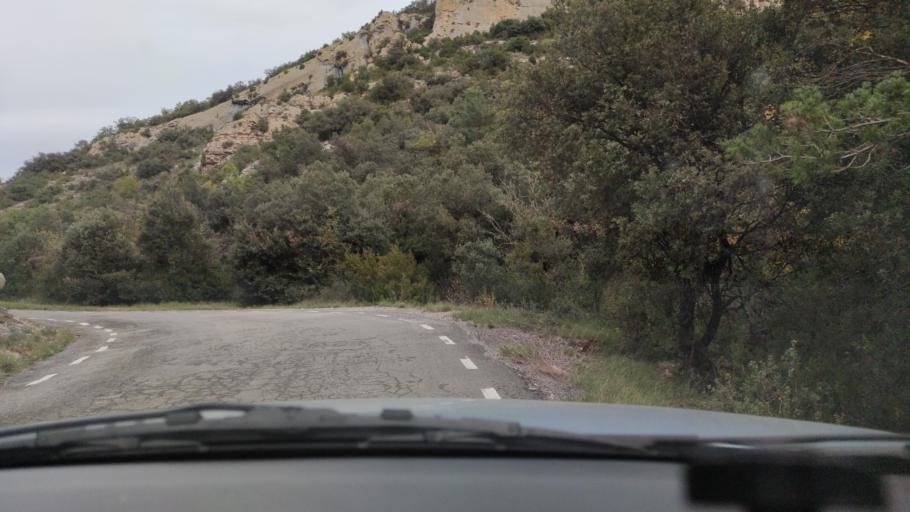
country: ES
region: Catalonia
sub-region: Provincia de Lleida
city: Llimiana
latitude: 42.0331
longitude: 1.0243
